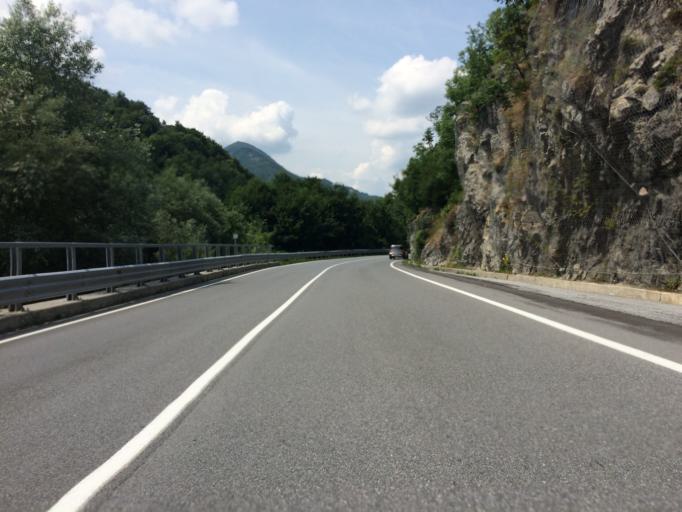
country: IT
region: Piedmont
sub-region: Provincia di Cuneo
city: Vernante
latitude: 44.2510
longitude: 7.5308
